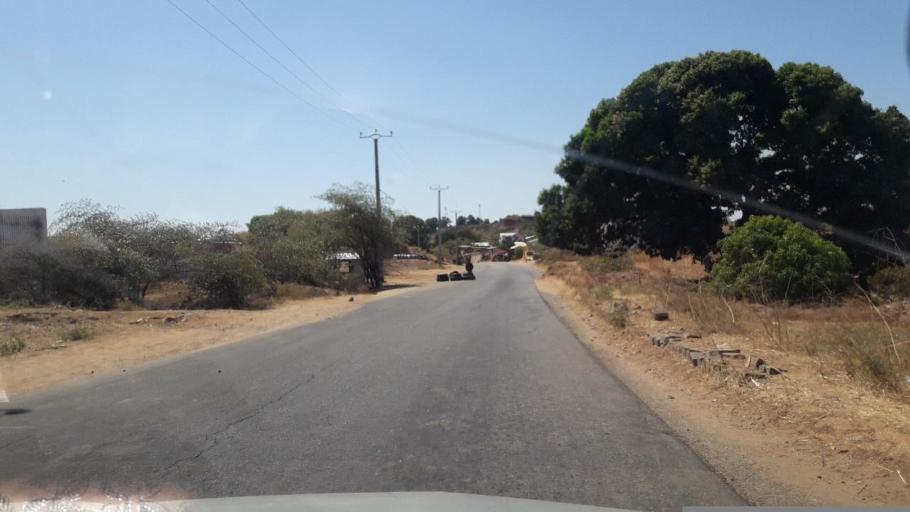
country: MG
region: Betsiboka
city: Maevatanana
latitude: -16.9505
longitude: 46.8448
